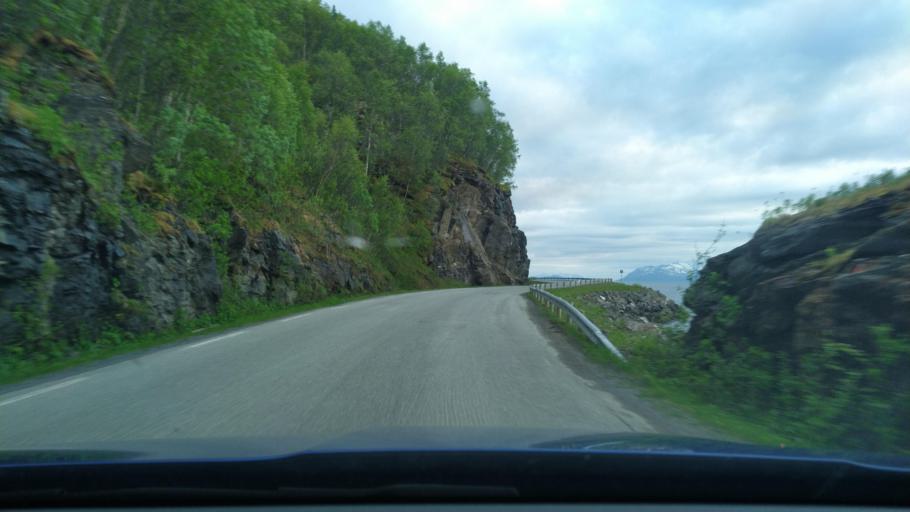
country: NO
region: Troms
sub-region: Lenvik
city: Finnsnes
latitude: 69.1460
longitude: 17.9320
